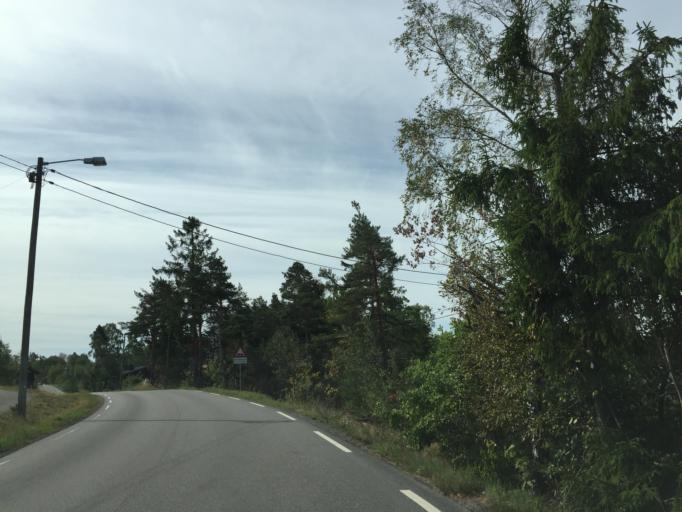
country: NO
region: Ostfold
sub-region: Moss
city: Moss
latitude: 59.5044
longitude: 10.6853
